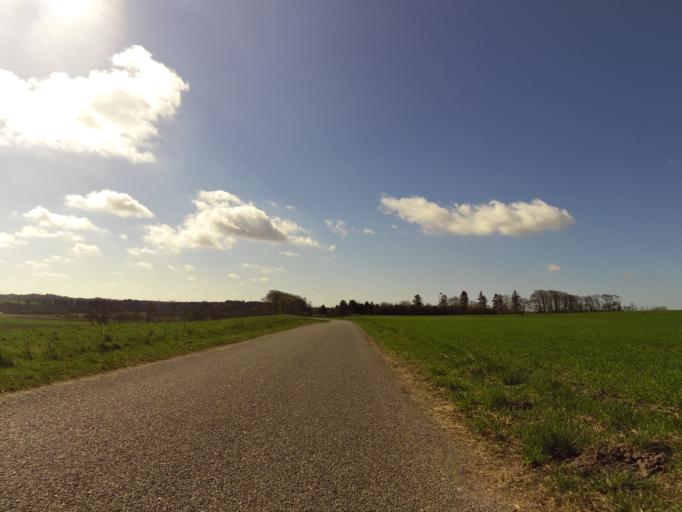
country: DK
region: Central Jutland
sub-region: Holstebro Kommune
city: Vinderup
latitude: 56.4312
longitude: 8.7323
